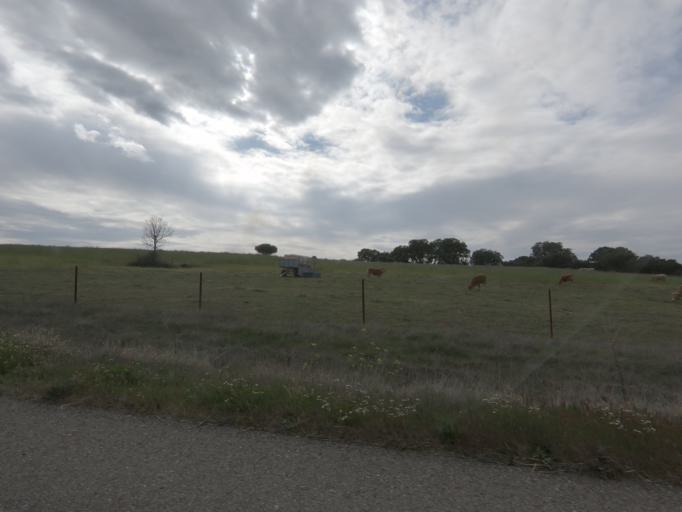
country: ES
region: Castille and Leon
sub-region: Provincia de Salamanca
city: Robleda
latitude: 40.3974
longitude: -6.6065
